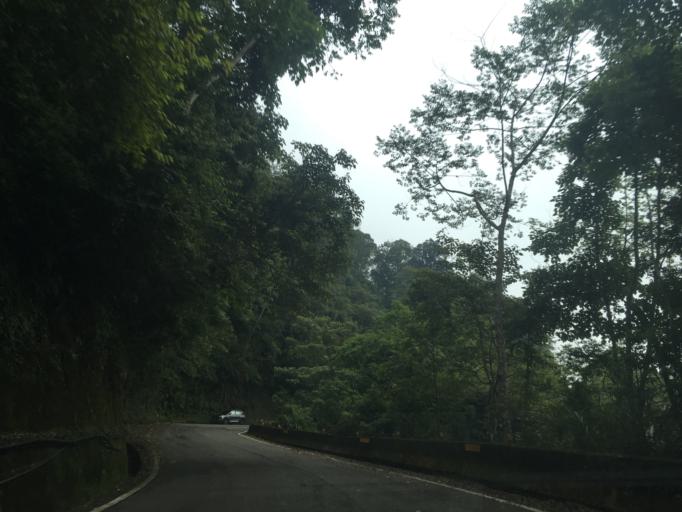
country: TW
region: Taiwan
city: Fengyuan
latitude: 24.2481
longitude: 120.9187
